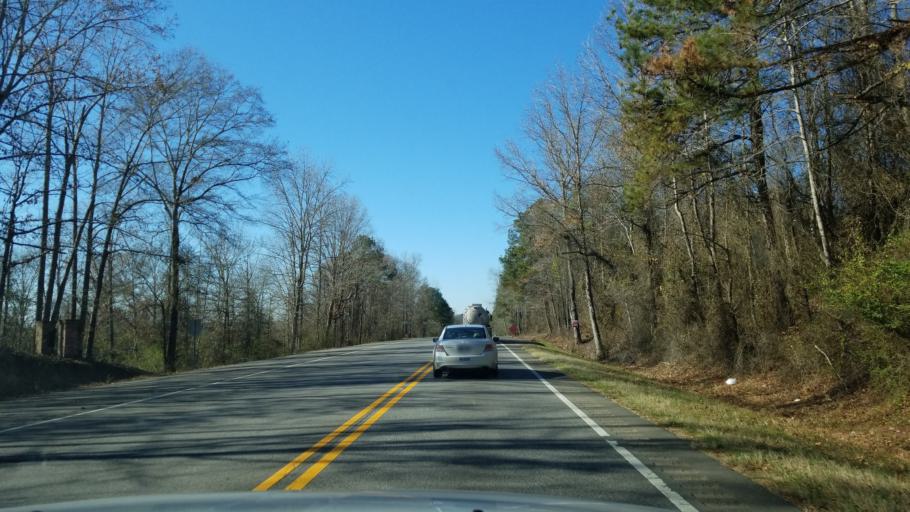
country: US
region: Alabama
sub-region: Pickens County
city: Gordo
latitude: 33.3323
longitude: -87.9172
